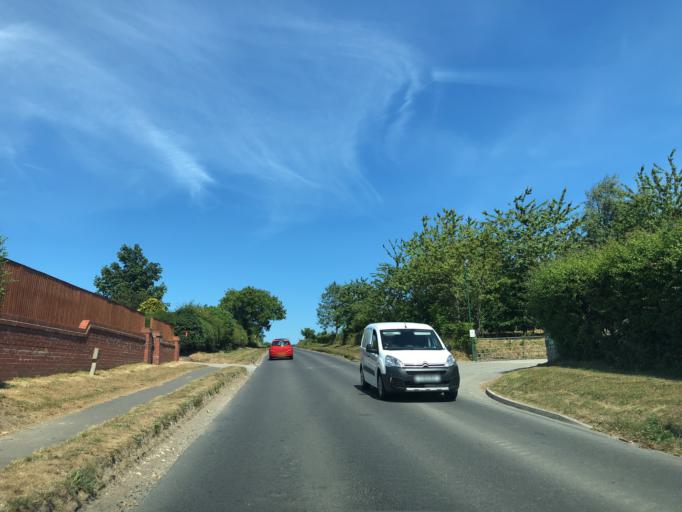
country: GB
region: England
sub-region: North Yorkshire
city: East Ayton
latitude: 54.2459
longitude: -0.4357
